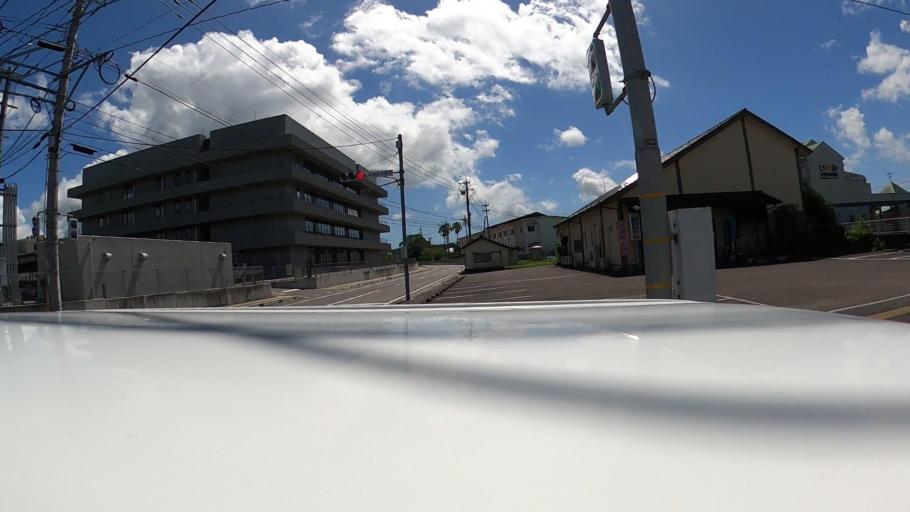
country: JP
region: Miyazaki
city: Tsuma
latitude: 32.1075
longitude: 131.4002
